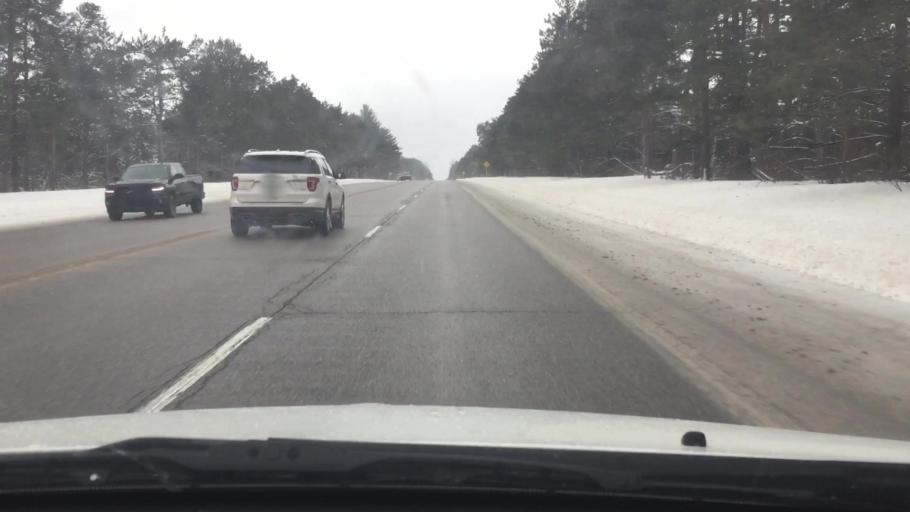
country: US
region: Michigan
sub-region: Otsego County
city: Gaylord
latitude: 45.0622
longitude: -84.8315
